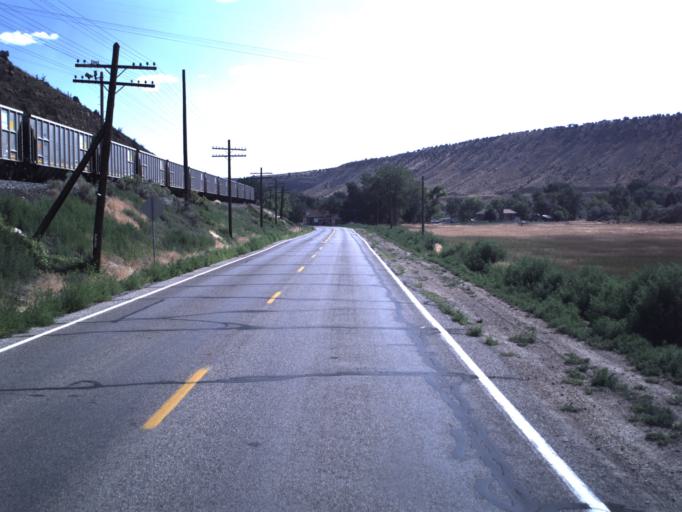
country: US
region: Utah
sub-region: Carbon County
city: Helper
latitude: 39.6781
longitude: -110.8570
